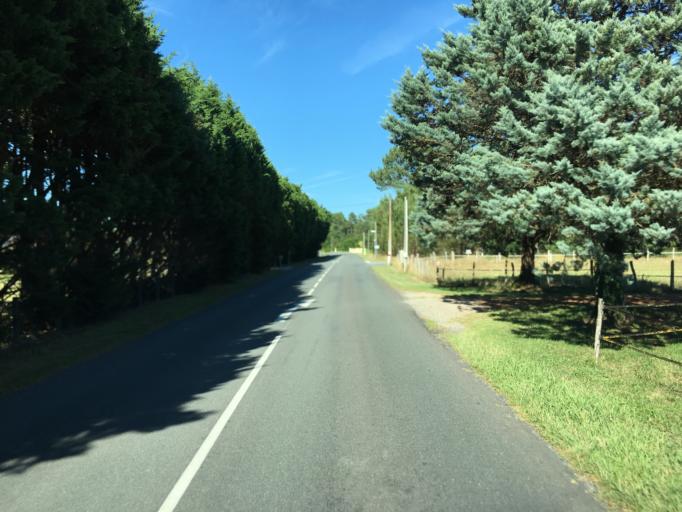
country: FR
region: Aquitaine
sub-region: Departement de la Gironde
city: Belin-Beliet
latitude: 44.5118
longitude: -0.7705
